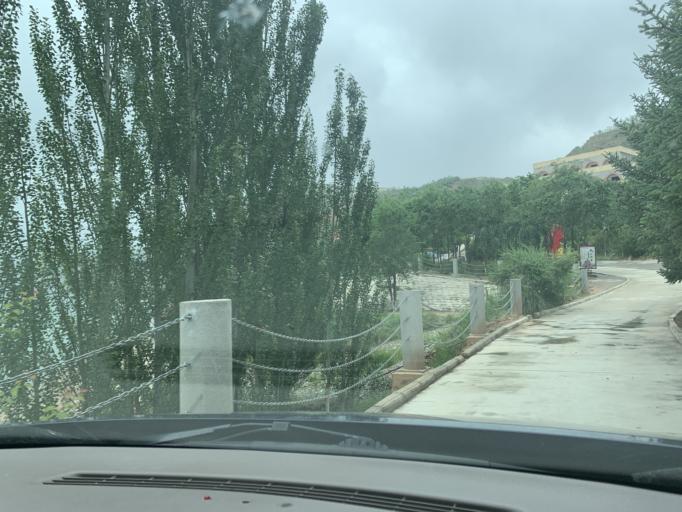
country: CN
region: Gansu Sheng
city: Gulang
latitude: 37.5626
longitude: 102.7426
